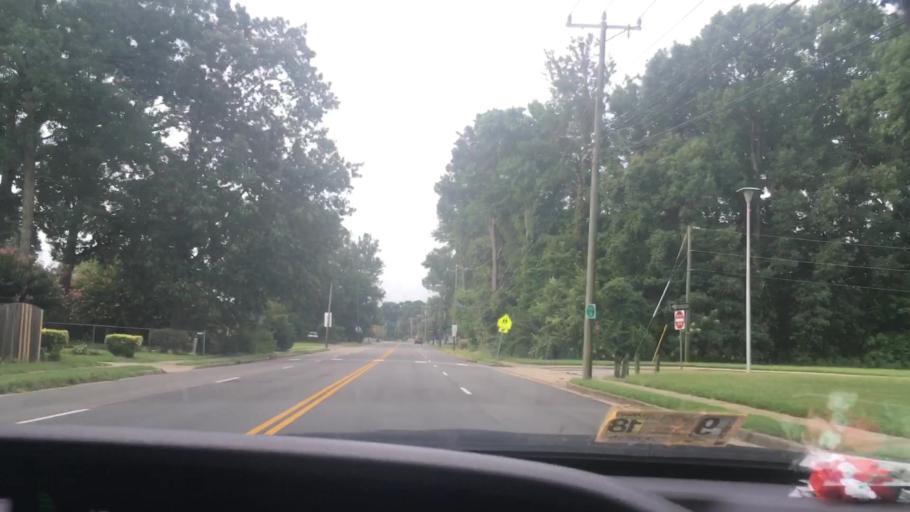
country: US
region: Virginia
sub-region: City of Hampton
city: East Hampton
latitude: 37.0403
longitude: -76.3218
